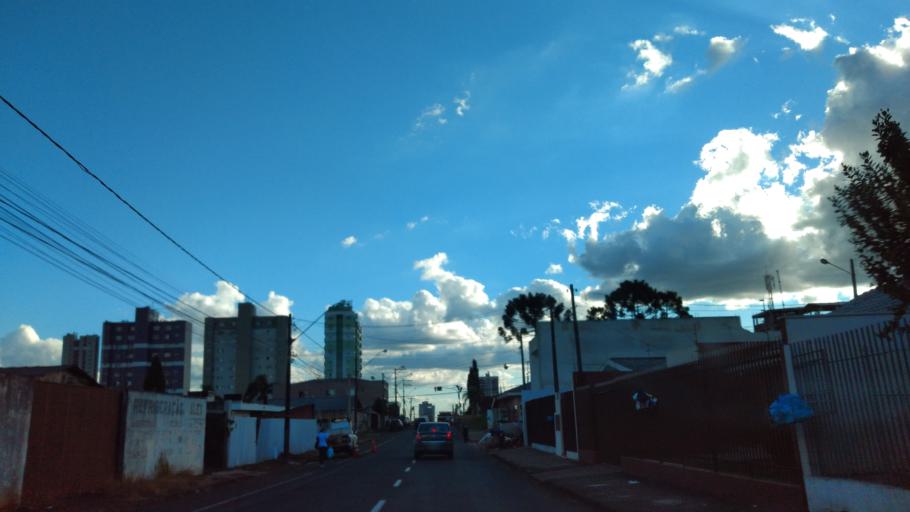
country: BR
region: Parana
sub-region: Guarapuava
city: Guarapuava
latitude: -25.3865
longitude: -51.4619
